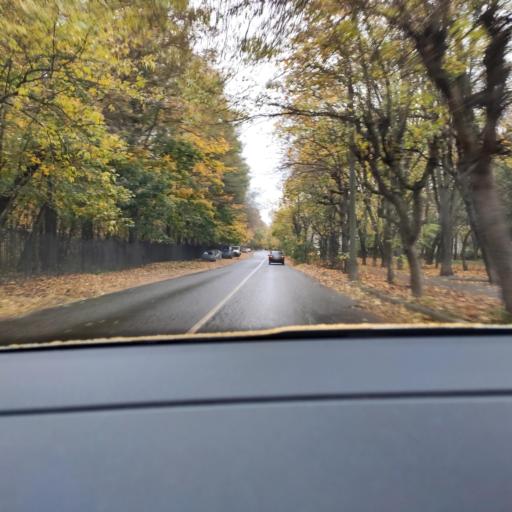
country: RU
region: Moskovskaya
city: Ivanteyevka
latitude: 55.9738
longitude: 37.8989
